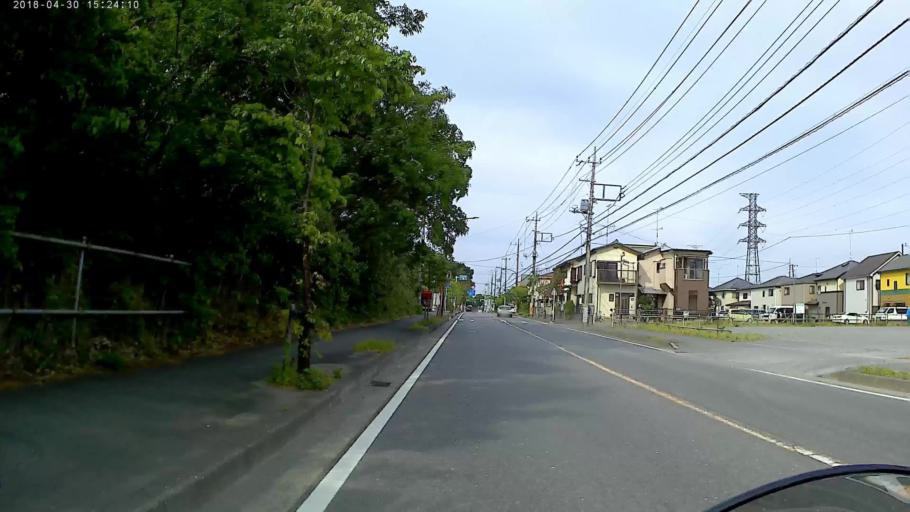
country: JP
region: Tokyo
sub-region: Machida-shi
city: Machida
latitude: 35.5529
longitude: 139.3940
